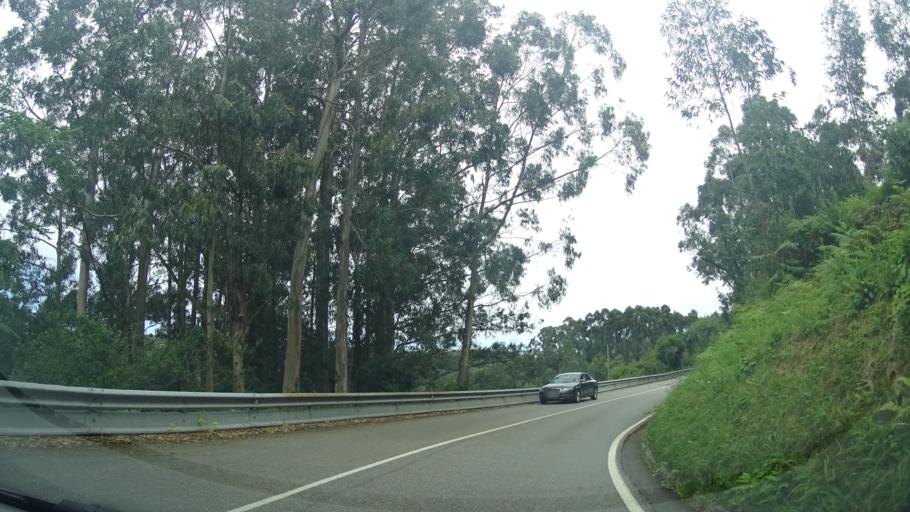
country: ES
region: Asturias
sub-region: Province of Asturias
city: Ribadesella
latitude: 43.4637
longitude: -5.0949
